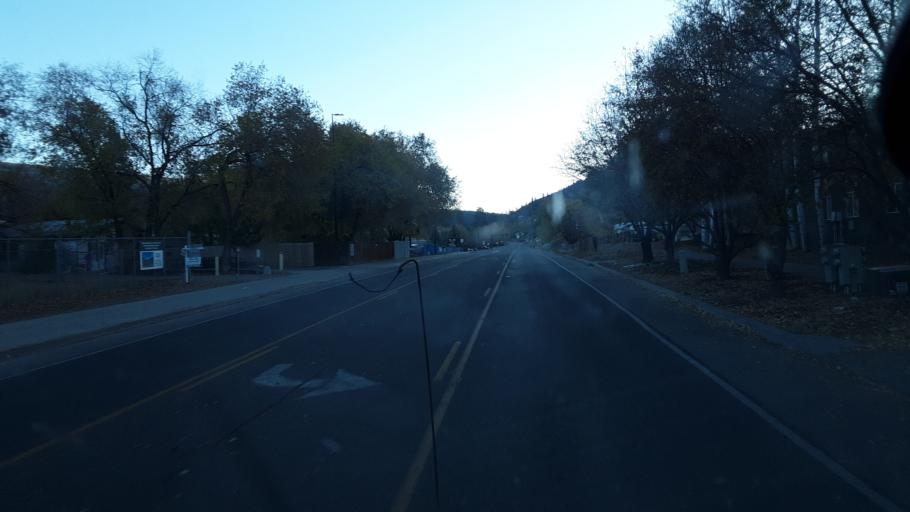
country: US
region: Colorado
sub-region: La Plata County
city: Durango
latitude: 37.2964
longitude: -107.8522
